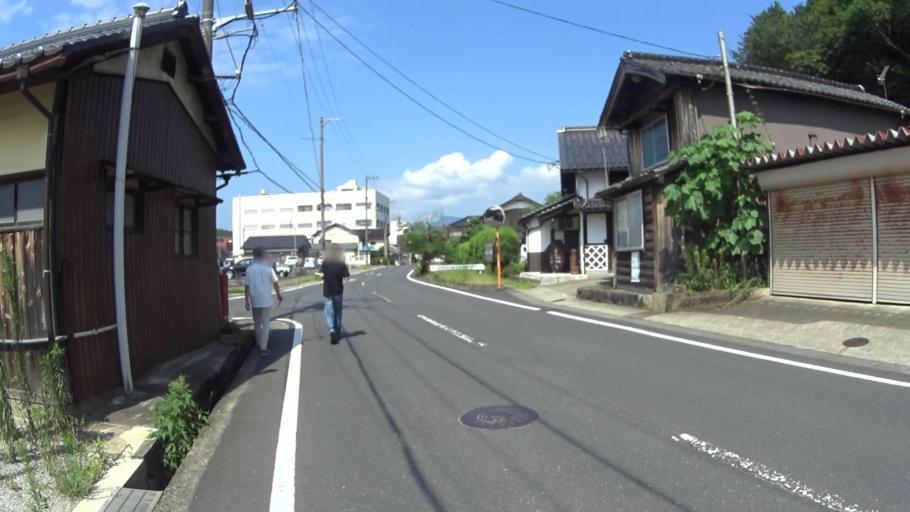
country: JP
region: Kyoto
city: Miyazu
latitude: 35.6229
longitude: 135.0613
